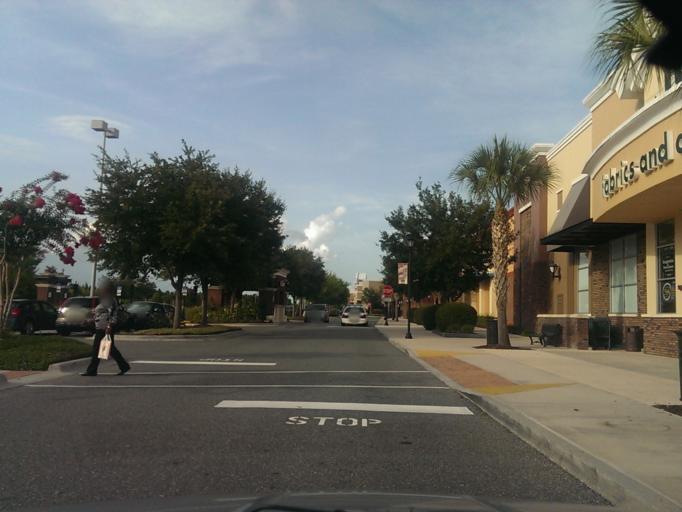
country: US
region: Florida
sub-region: Orange County
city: Winter Garden
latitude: 28.5226
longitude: -81.5820
